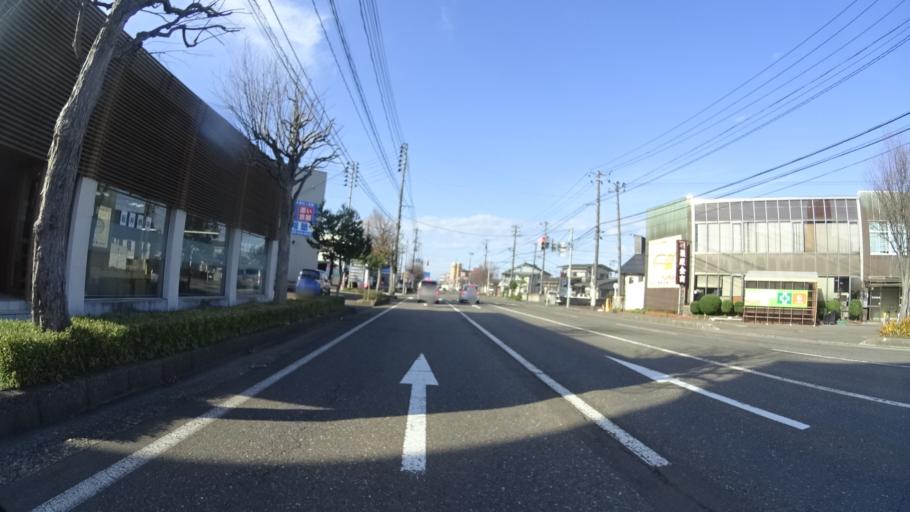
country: JP
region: Niigata
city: Joetsu
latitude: 37.1229
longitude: 138.2514
